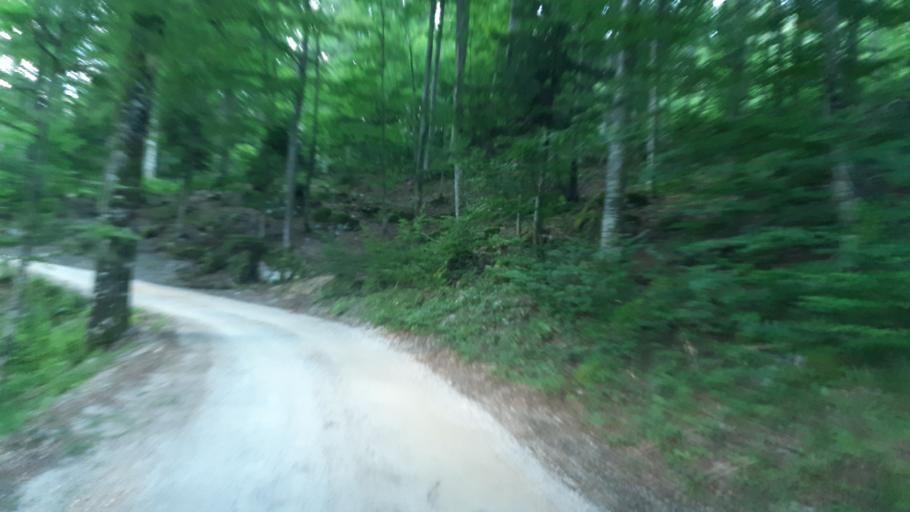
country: SI
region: Dolenjske Toplice
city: Dolenjske Toplice
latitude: 45.6852
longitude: 15.0073
